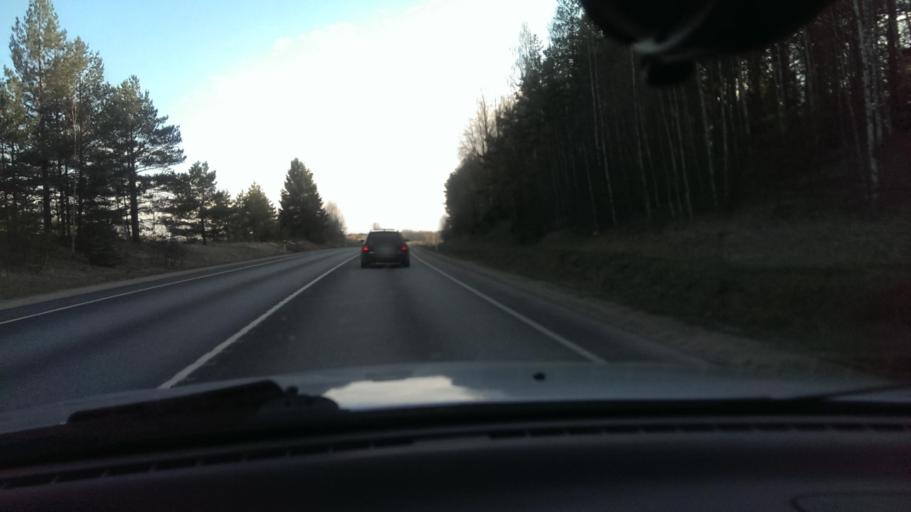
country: EE
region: Tartu
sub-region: UElenurme vald
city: Ulenurme
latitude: 58.2002
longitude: 26.7055
